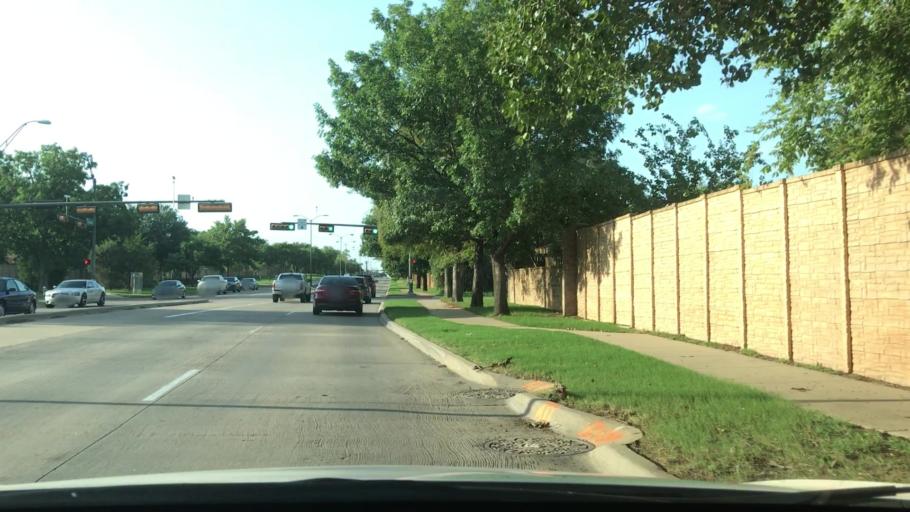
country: US
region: Texas
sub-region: Tarrant County
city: Euless
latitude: 32.8463
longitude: -97.0825
